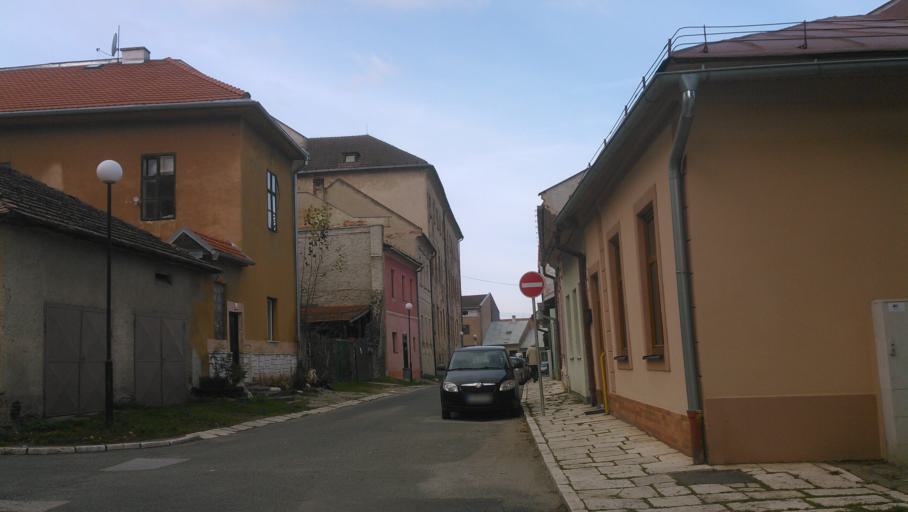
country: SK
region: Presovsky
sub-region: Okres Presov
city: Levoca
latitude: 49.0281
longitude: 20.5914
